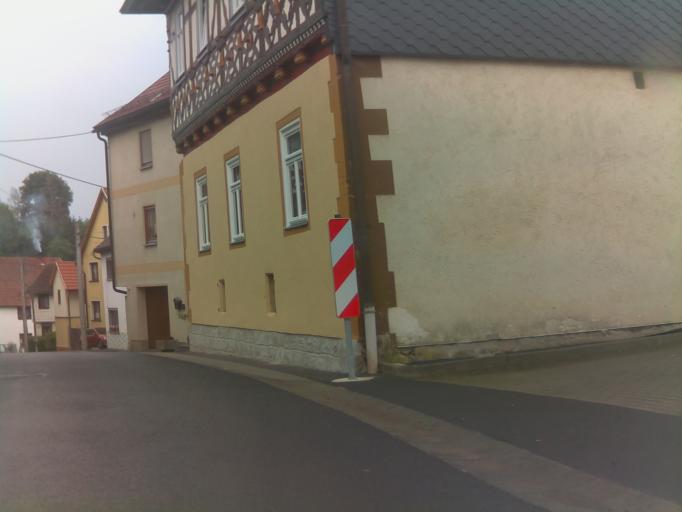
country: DE
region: Thuringia
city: Marisfeld
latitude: 50.5554
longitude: 10.5710
